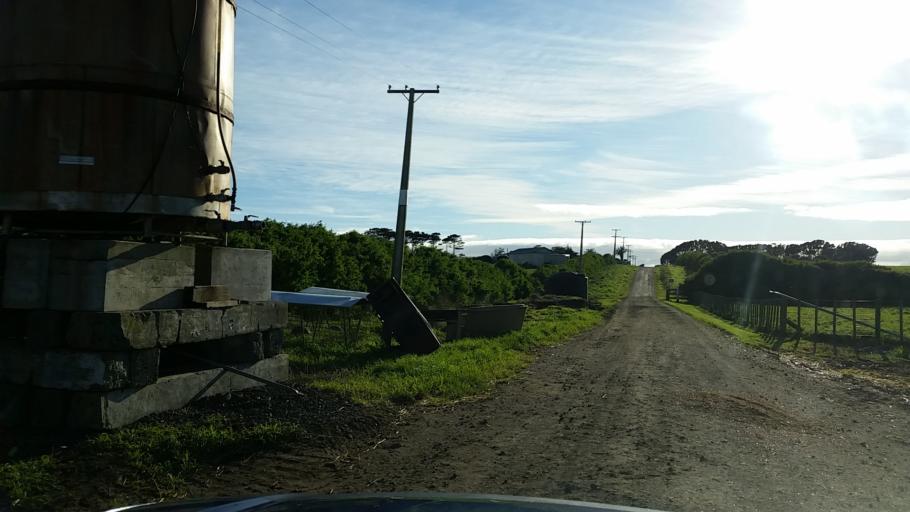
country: NZ
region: Taranaki
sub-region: South Taranaki District
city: Patea
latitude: -39.7165
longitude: 174.4267
